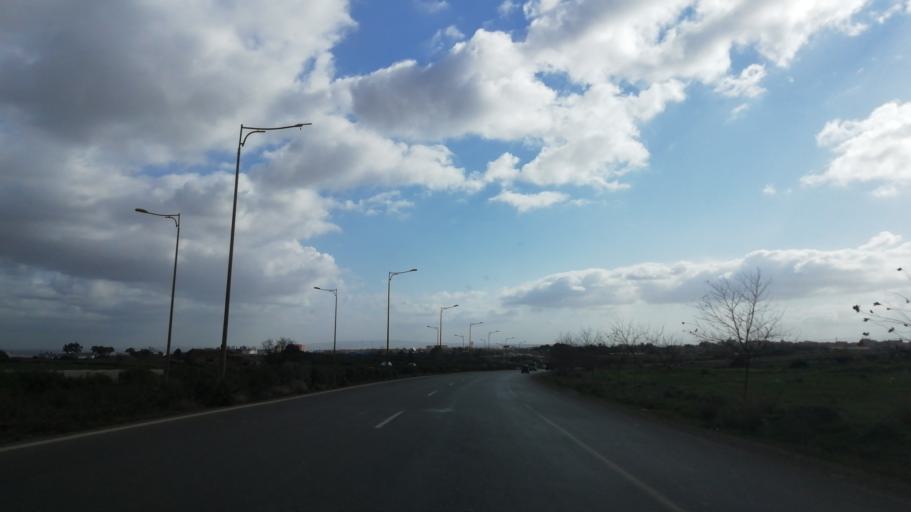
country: DZ
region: Oran
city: Oran
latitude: 35.6525
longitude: -0.6807
